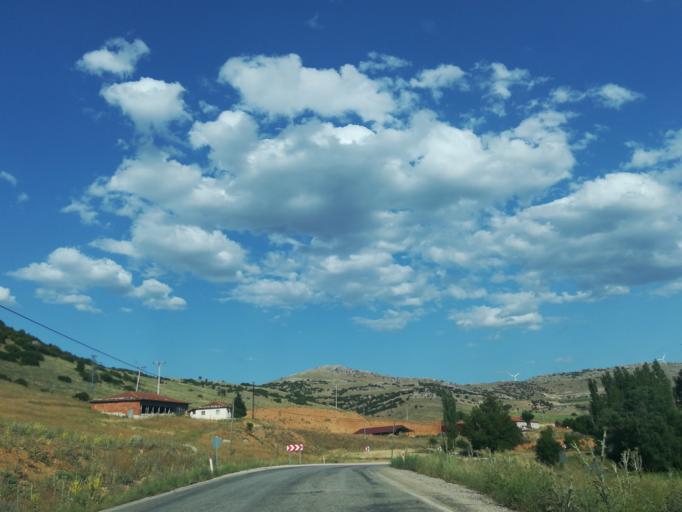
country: TR
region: Afyonkarahisar
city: Dinar
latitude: 38.0990
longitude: 30.1551
